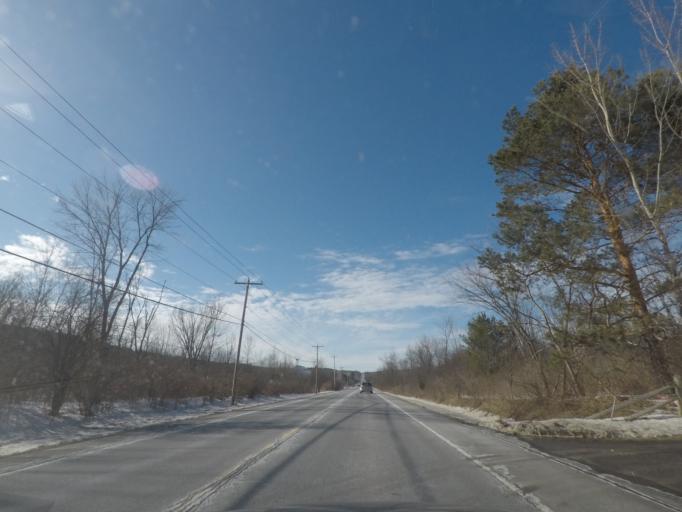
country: US
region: New York
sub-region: Albany County
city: Altamont
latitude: 42.7419
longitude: -74.0219
